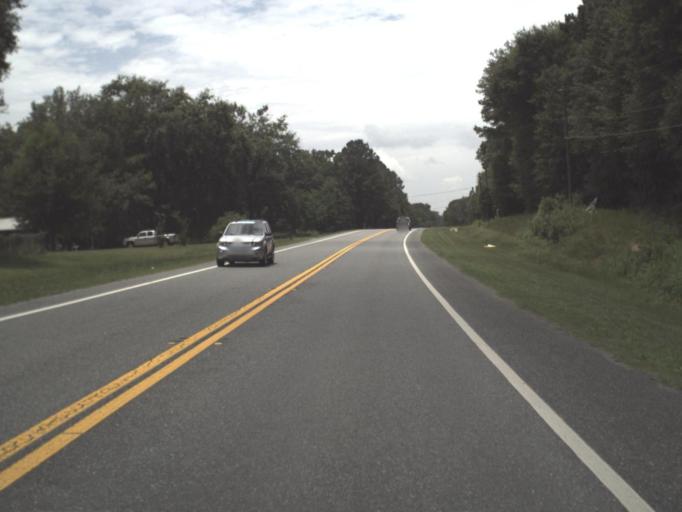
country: US
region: Florida
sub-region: Madison County
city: Madison
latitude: 30.4433
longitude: -83.4284
